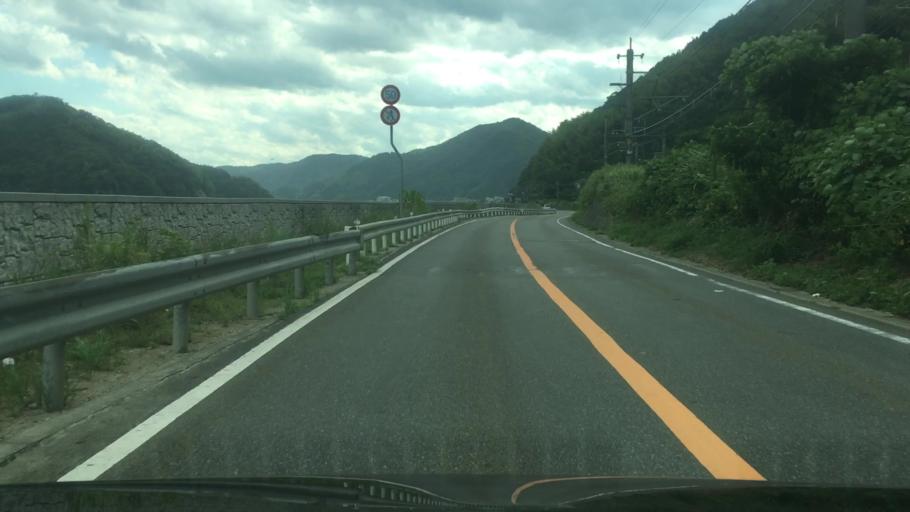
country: JP
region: Hyogo
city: Toyooka
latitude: 35.6167
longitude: 134.8102
